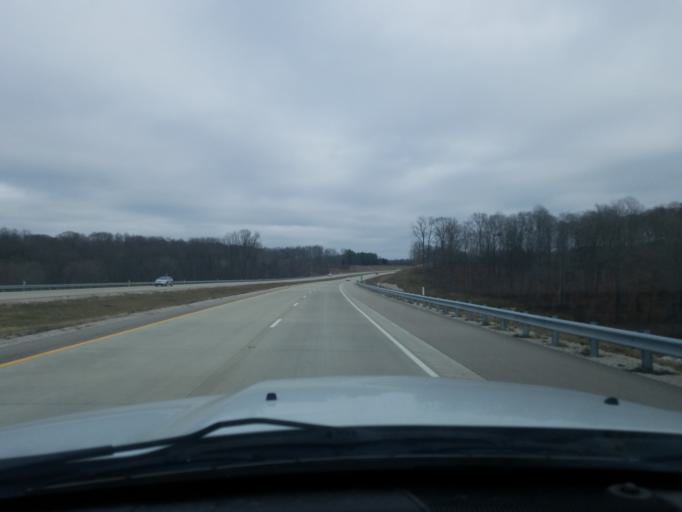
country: US
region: Indiana
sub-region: Monroe County
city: Bloomington
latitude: 39.0731
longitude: -86.6572
